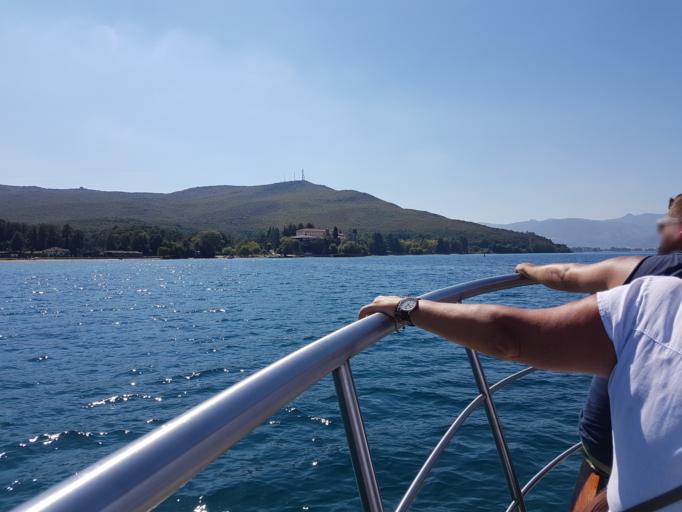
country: AL
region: Korce
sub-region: Rrethi i Pogradecit
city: Bucimas
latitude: 40.9181
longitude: 20.7438
